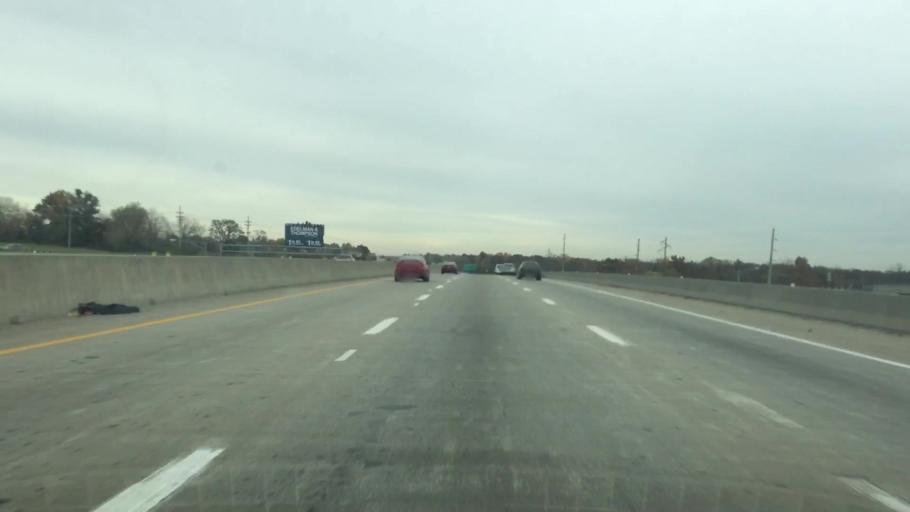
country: US
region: Missouri
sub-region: Jackson County
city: Grandview
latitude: 38.8575
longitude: -94.5281
